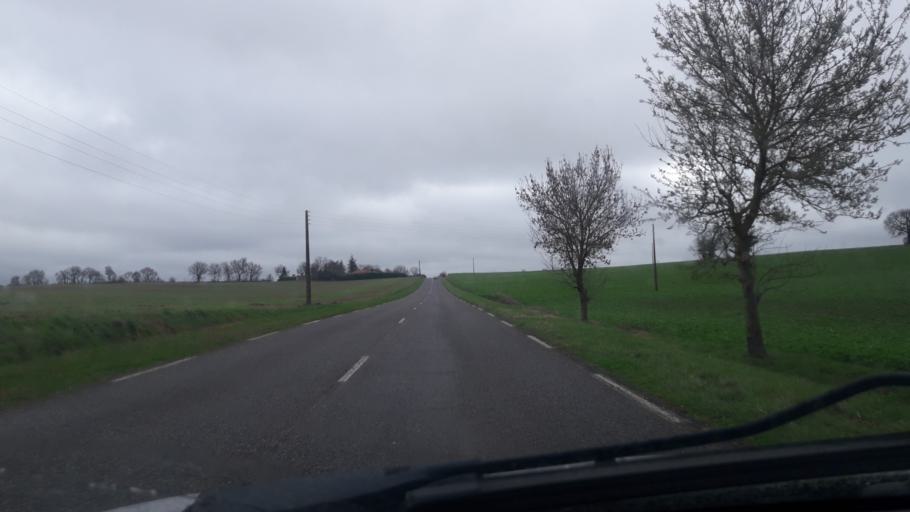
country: FR
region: Midi-Pyrenees
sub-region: Departement du Gers
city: Gimont
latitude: 43.7071
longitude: 0.9914
